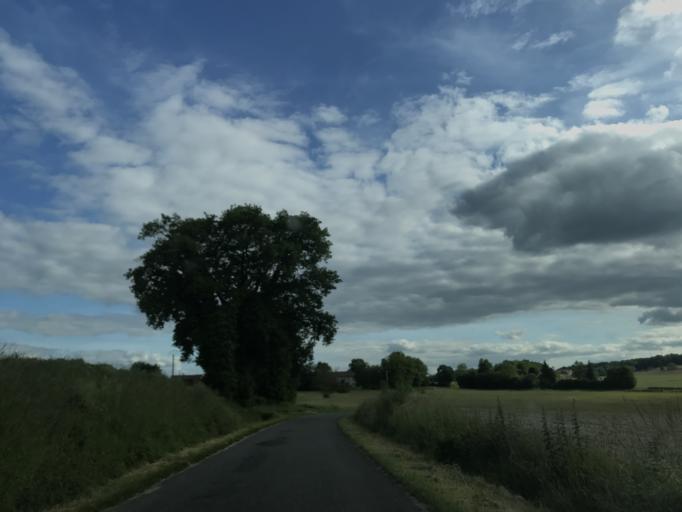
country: FR
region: Aquitaine
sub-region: Departement de la Dordogne
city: Saint-Aulaye
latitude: 45.2541
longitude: 0.1309
